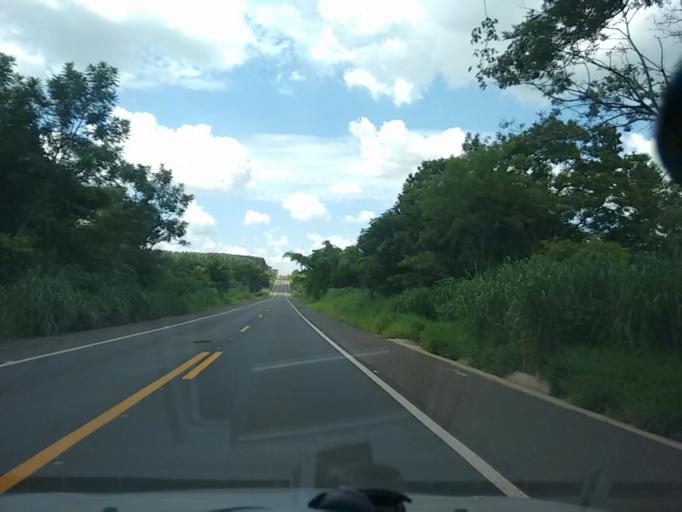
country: BR
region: Sao Paulo
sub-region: Osvaldo Cruz
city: Osvaldo Cruz
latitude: -21.8415
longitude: -50.8287
